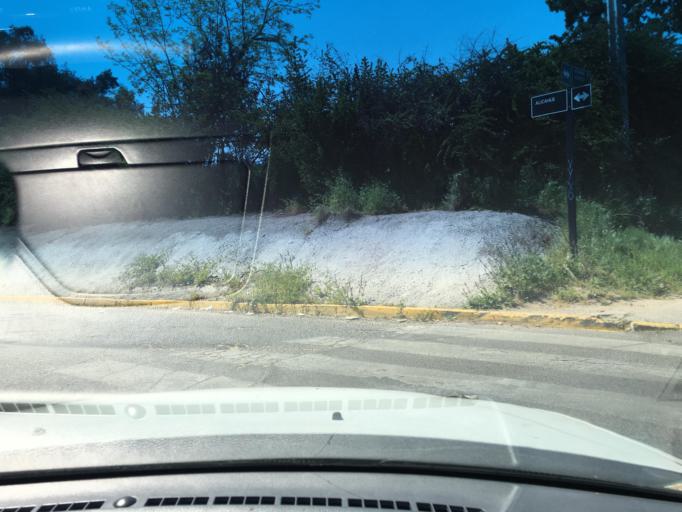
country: CL
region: Santiago Metropolitan
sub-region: Provincia de Santiago
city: Villa Presidente Frei, Nunoa, Santiago, Chile
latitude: -33.5274
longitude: -70.5689
